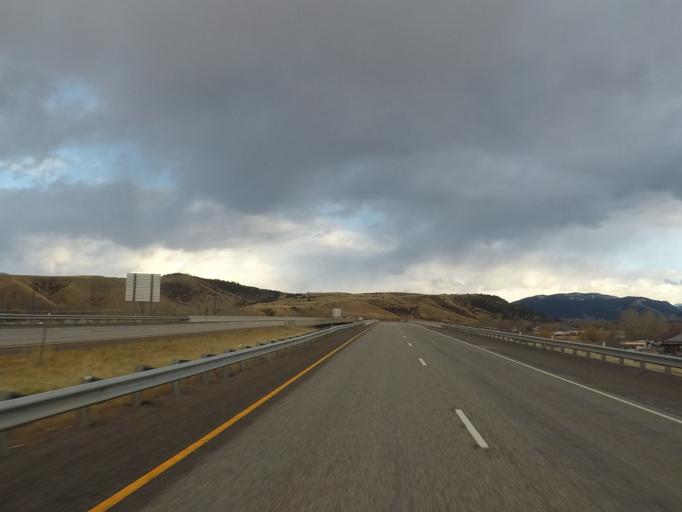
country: US
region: Montana
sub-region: Gallatin County
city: Bozeman
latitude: 45.6941
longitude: -111.0335
